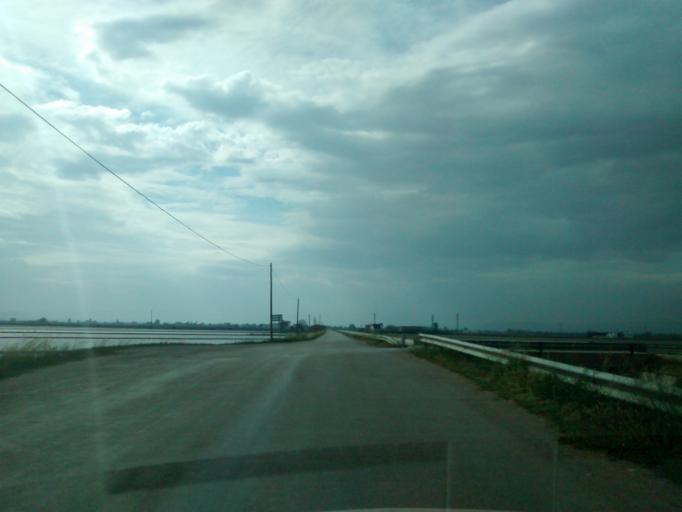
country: ES
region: Catalonia
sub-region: Provincia de Tarragona
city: Deltebre
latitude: 40.6966
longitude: 0.7599
